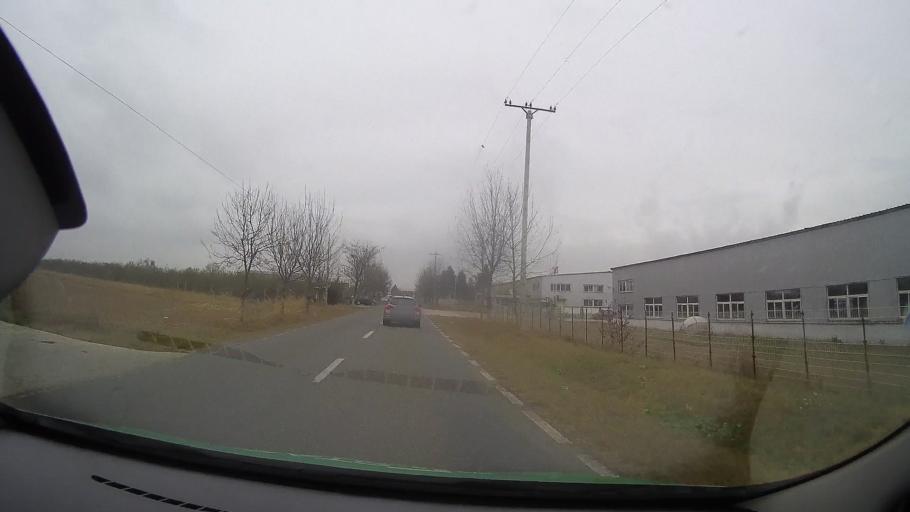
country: RO
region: Prahova
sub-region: Oras Baicoi
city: Liliesti
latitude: 45.0154
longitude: 25.8850
